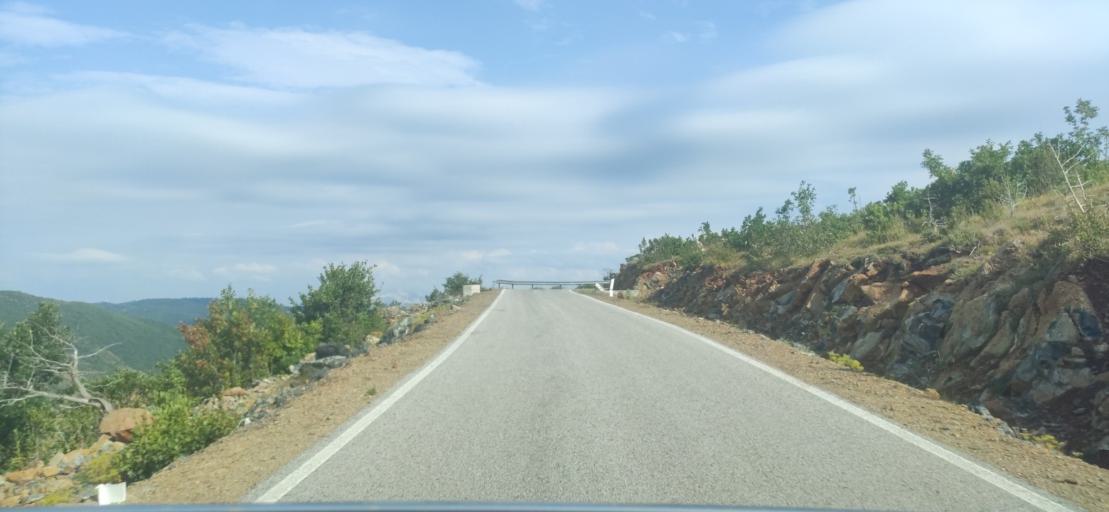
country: AL
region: Shkoder
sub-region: Rrethi i Pukes
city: Iballe
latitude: 42.1720
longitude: 20.0036
